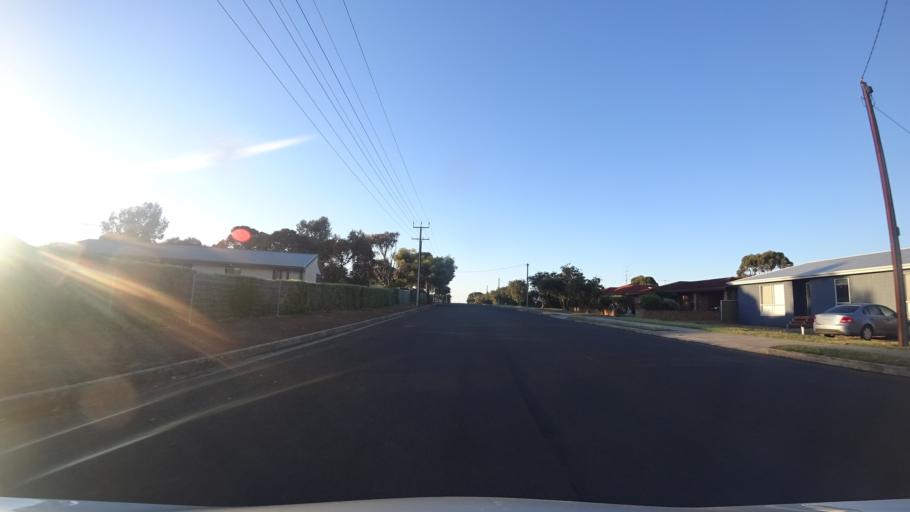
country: AU
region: South Australia
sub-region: Kangaroo Island
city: Kingscote
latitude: -35.6555
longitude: 137.6341
